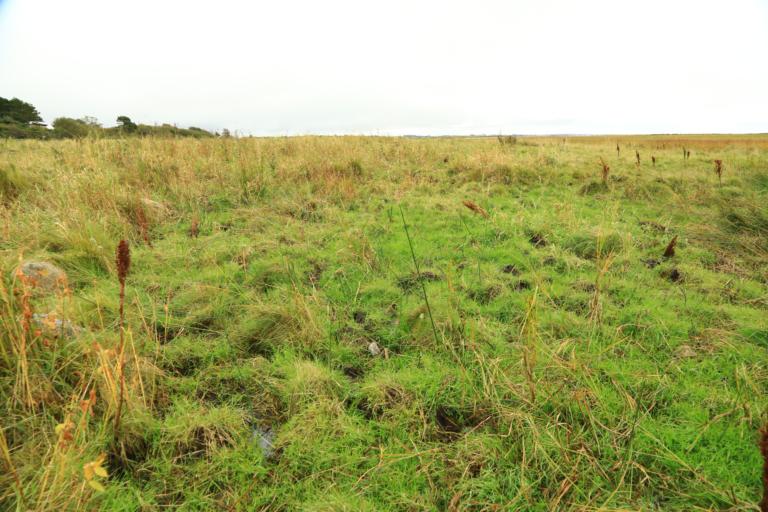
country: SE
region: Halland
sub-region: Varbergs Kommun
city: Tvaaker
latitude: 57.0195
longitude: 12.3379
